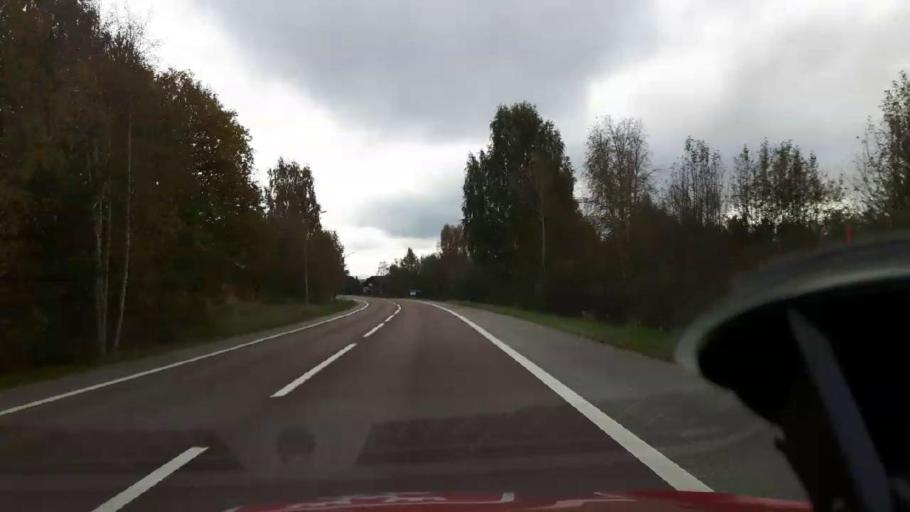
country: SE
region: Jaemtland
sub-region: Harjedalens Kommun
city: Sveg
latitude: 62.1761
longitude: 14.9149
